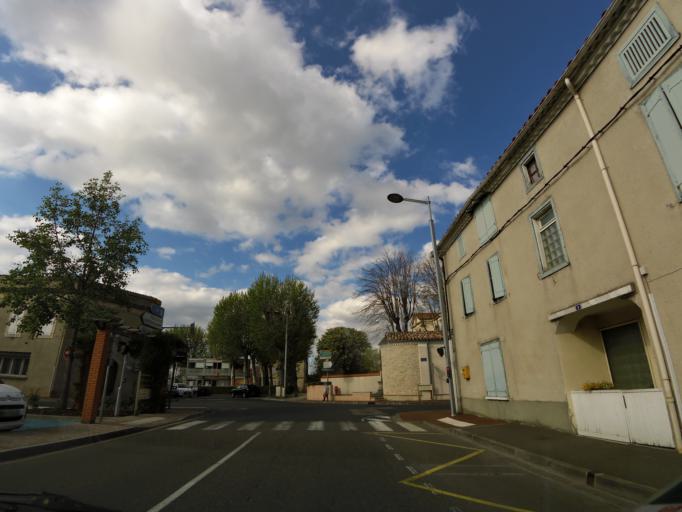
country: FR
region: Midi-Pyrenees
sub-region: Departement de la Haute-Garonne
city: Revel
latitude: 43.4580
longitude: 2.0069
